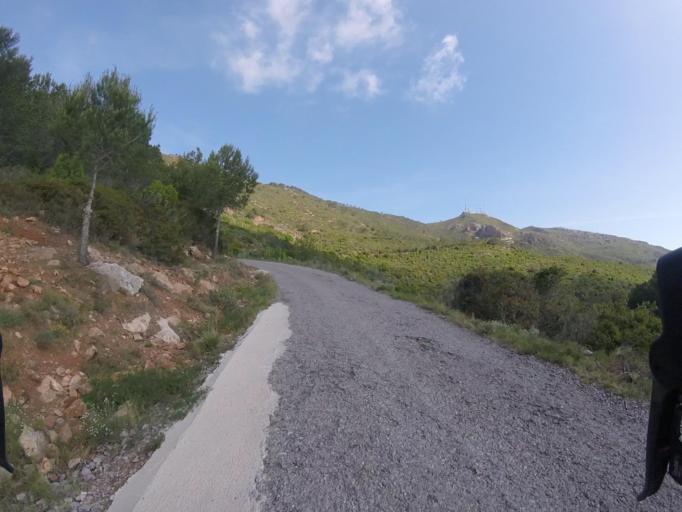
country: ES
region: Valencia
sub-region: Provincia de Castello
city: Benicassim
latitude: 40.0757
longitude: 0.0261
